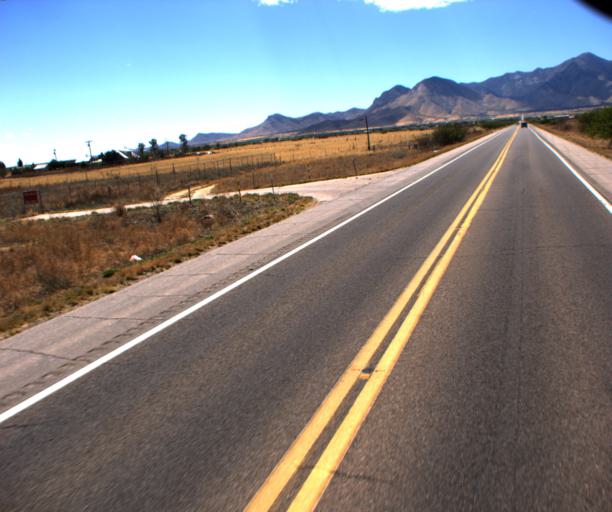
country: US
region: Arizona
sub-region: Cochise County
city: Sierra Vista Southeast
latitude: 31.3800
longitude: -110.1361
